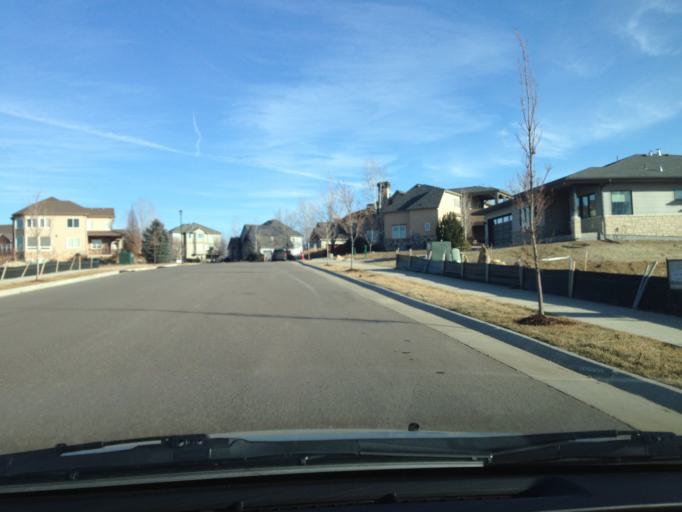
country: US
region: Colorado
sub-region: Boulder County
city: Erie
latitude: 40.0407
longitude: -105.0846
